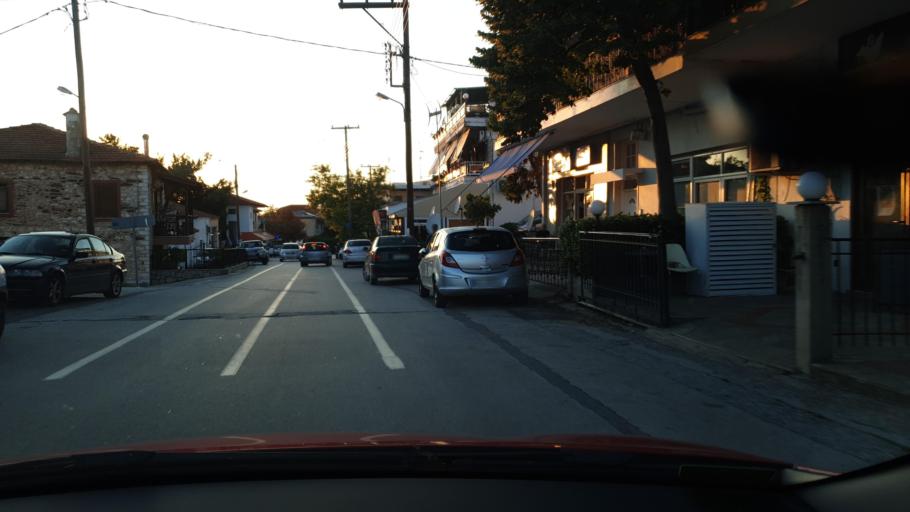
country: GR
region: Central Macedonia
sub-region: Nomos Chalkidikis
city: Galatista
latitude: 40.4666
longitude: 23.2797
